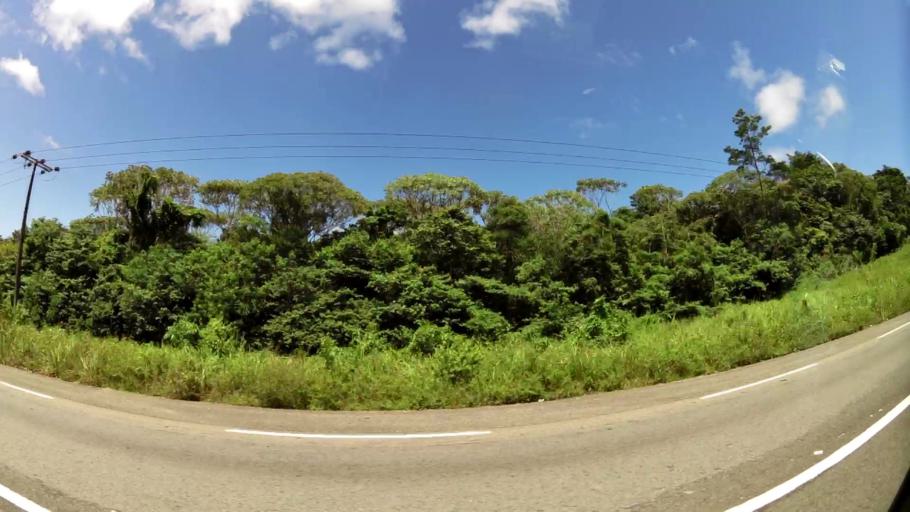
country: GF
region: Guyane
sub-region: Guyane
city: Matoury
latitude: 4.8666
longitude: -52.3347
